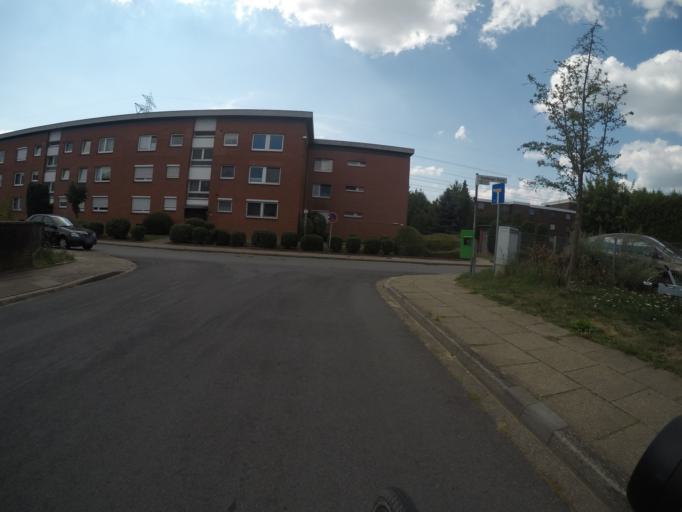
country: DE
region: Schleswig-Holstein
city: Oststeinbek
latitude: 53.5433
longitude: 10.1573
